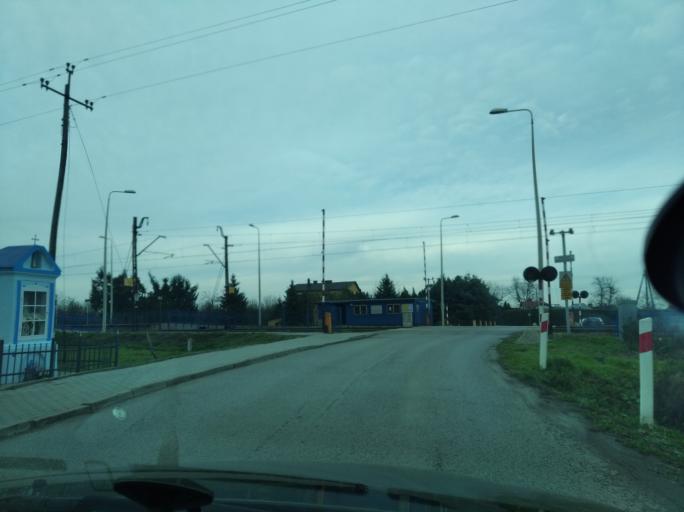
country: PL
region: Subcarpathian Voivodeship
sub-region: Powiat przeworski
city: Grzeska
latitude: 50.0795
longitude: 22.4544
